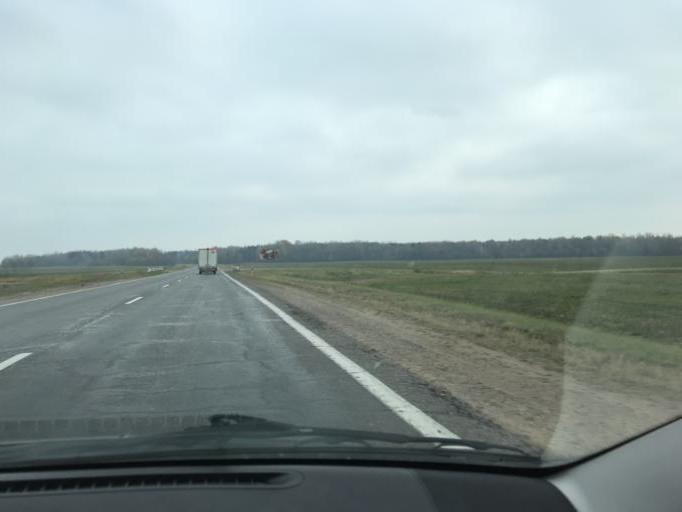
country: BY
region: Vitebsk
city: Chashniki
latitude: 55.0162
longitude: 29.4447
